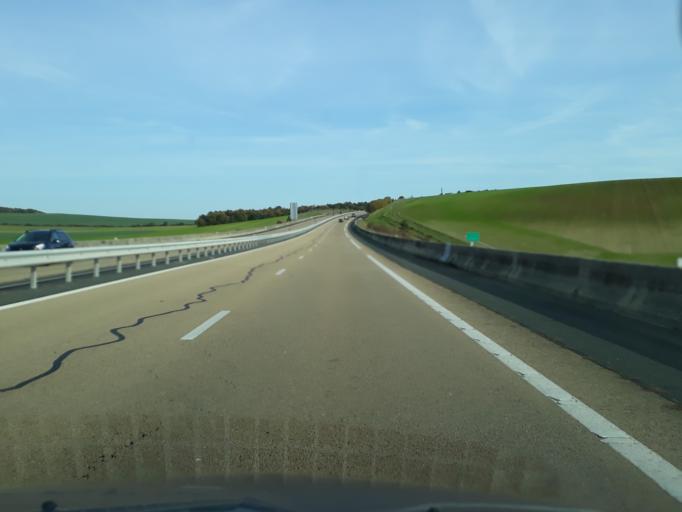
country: FR
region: Champagne-Ardenne
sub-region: Departement de l'Aube
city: Aix-en-Othe
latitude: 48.2625
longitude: 3.6793
